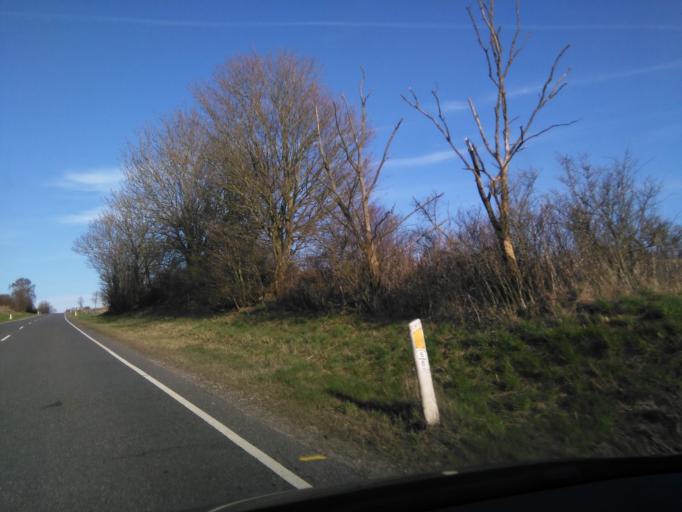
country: DK
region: Central Jutland
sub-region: Skanderborg Kommune
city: Skanderborg
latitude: 56.0259
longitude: 9.8424
